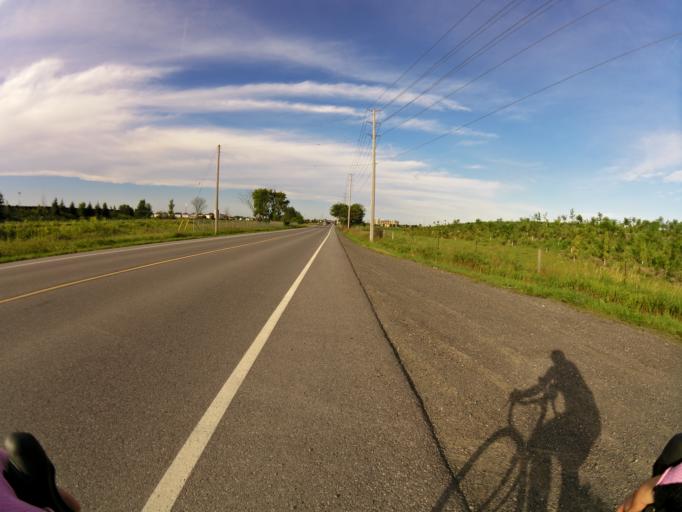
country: CA
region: Ontario
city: Bells Corners
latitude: 45.2578
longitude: -75.7778
